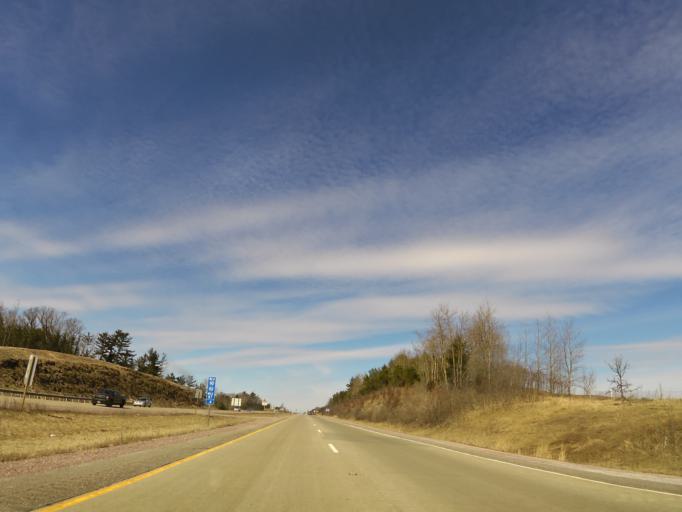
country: US
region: Wisconsin
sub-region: Sauk County
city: Lake Delton
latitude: 43.6284
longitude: -89.8059
